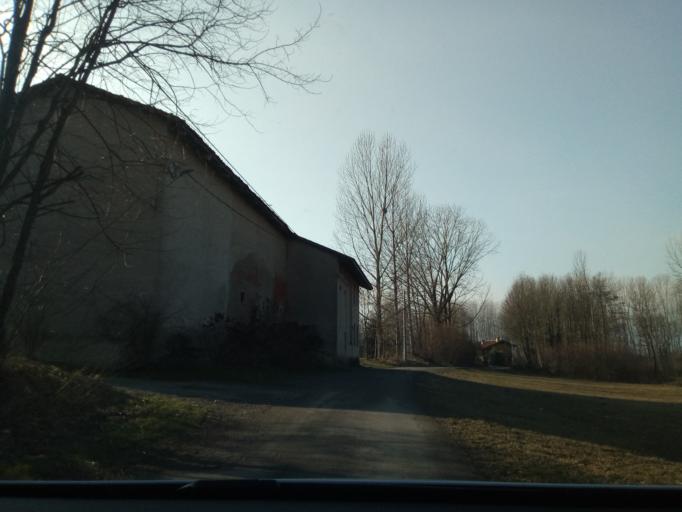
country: IT
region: Piedmont
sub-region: Provincia di Torino
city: Bollengo
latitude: 45.4532
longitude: 7.9312
